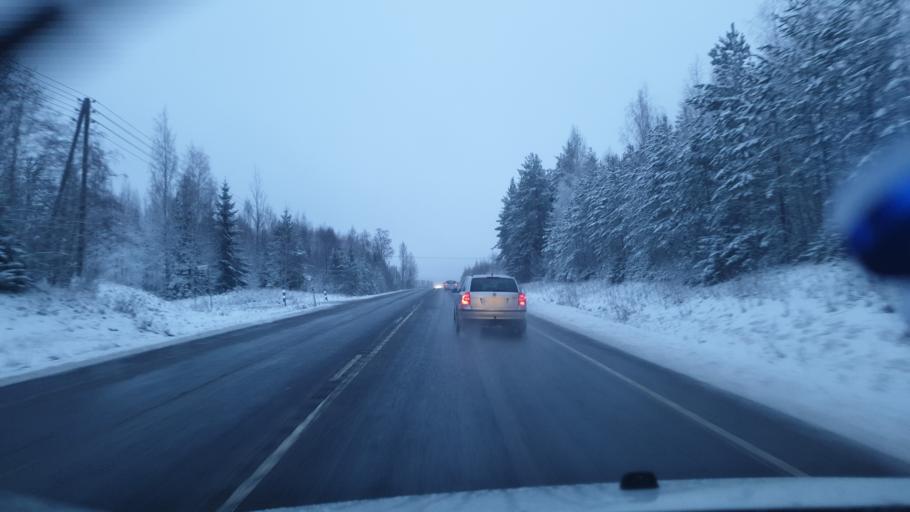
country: FI
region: Central Finland
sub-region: Saarijaervi-Viitasaari
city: Viitasaari
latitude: 63.1049
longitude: 25.8270
